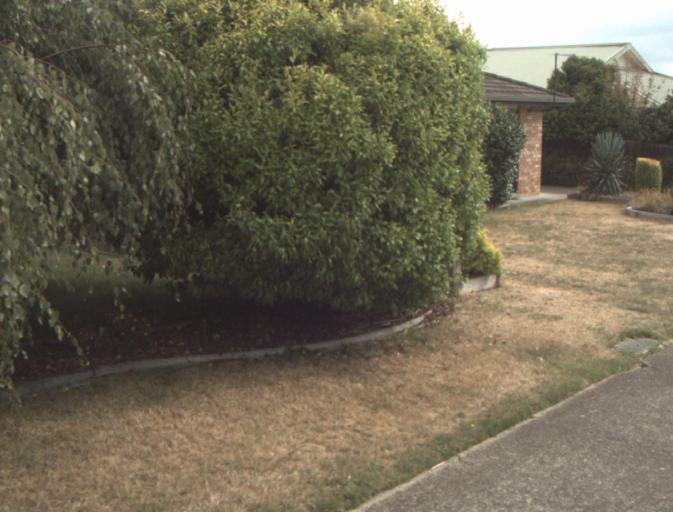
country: AU
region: Tasmania
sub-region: Launceston
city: Summerhill
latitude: -41.4806
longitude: 147.1724
